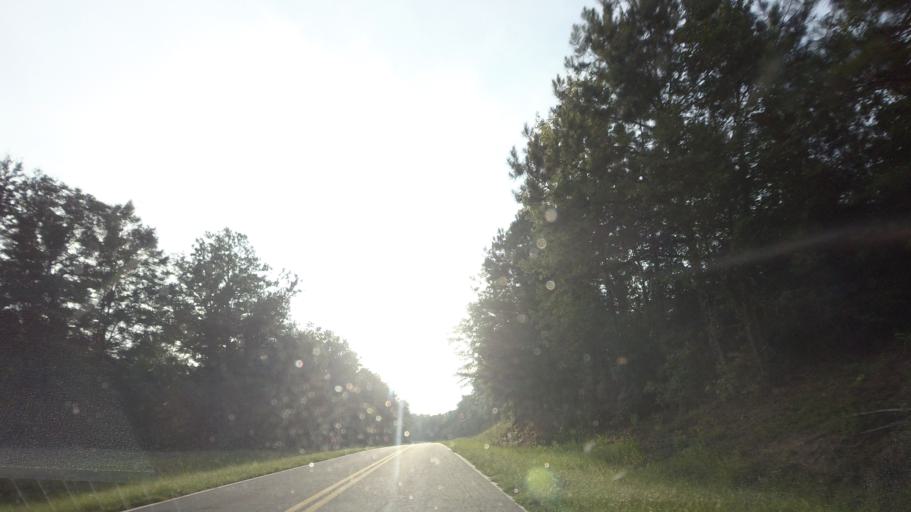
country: US
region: Georgia
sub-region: Wilkinson County
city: Gordon
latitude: 32.8349
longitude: -83.3650
